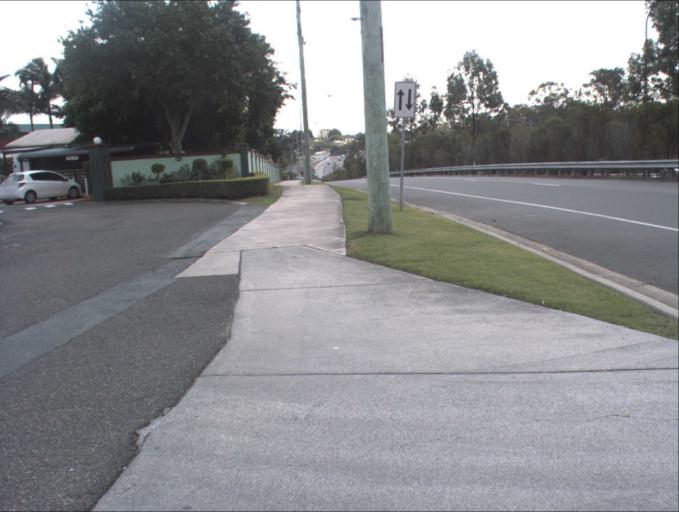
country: AU
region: Queensland
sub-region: Logan
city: Park Ridge South
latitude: -27.6920
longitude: 153.0342
